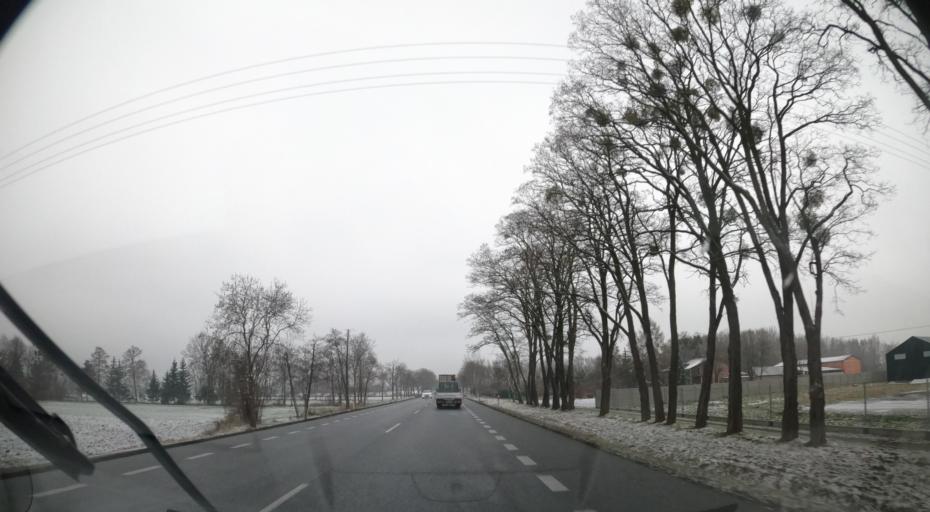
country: PL
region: Masovian Voivodeship
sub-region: Powiat sochaczewski
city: Teresin
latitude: 52.2152
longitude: 20.3948
